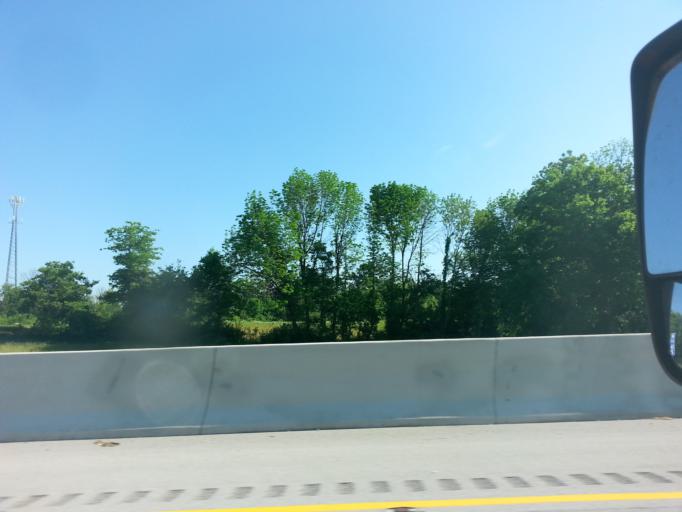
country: US
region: Kentucky
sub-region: Shelby County
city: Simpsonville
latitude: 38.2114
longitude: -85.3714
